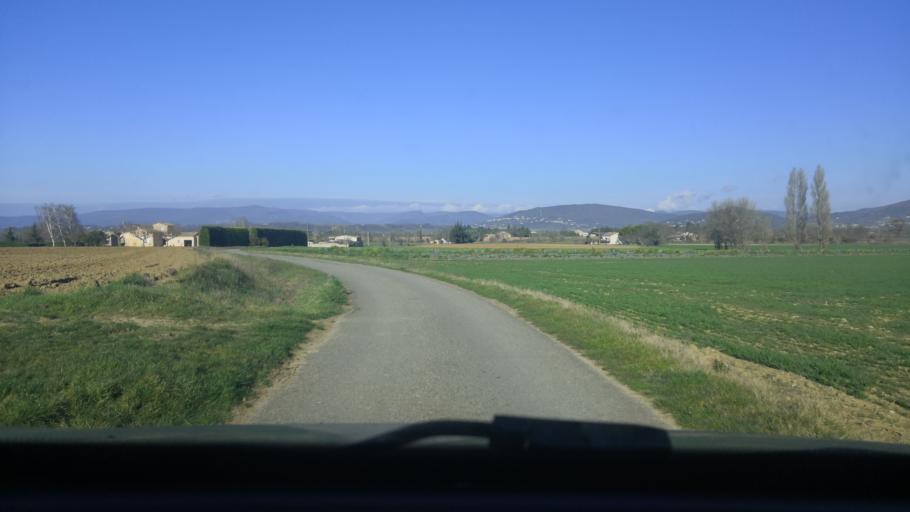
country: FR
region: Rhone-Alpes
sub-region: Departement de la Drome
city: Sauzet
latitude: 44.5710
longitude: 4.8422
